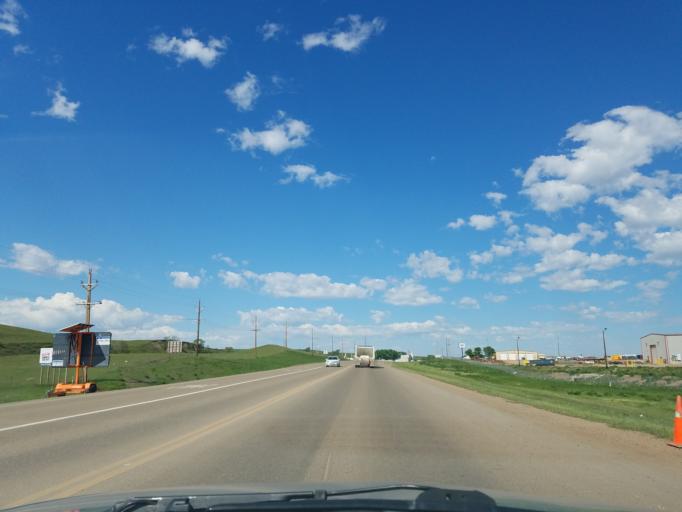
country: US
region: North Dakota
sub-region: McKenzie County
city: Watford City
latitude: 47.7983
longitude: -103.2984
